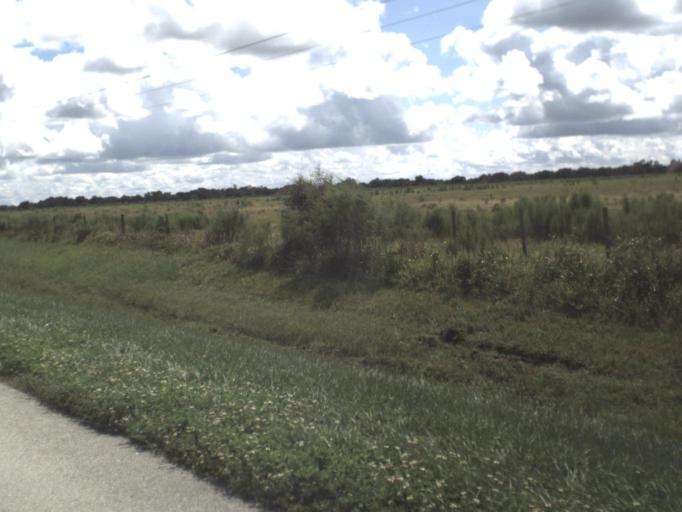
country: US
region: Florida
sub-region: DeSoto County
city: Arcadia
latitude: 27.2506
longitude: -81.9568
